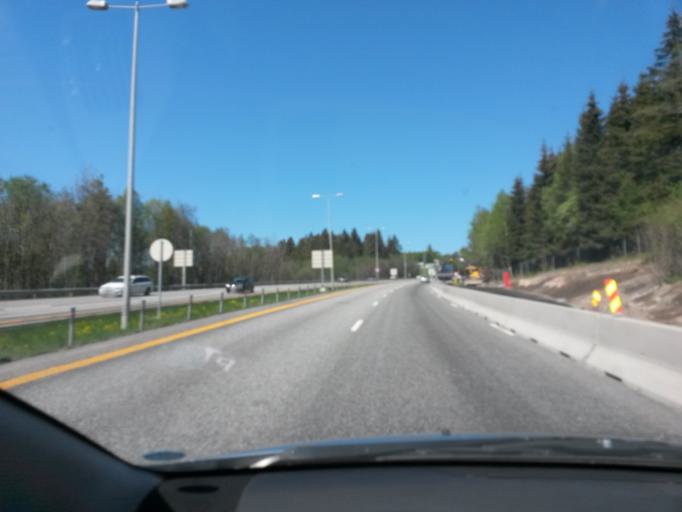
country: NO
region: Buskerud
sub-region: Lier
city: Tranby
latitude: 59.7977
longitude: 10.2678
